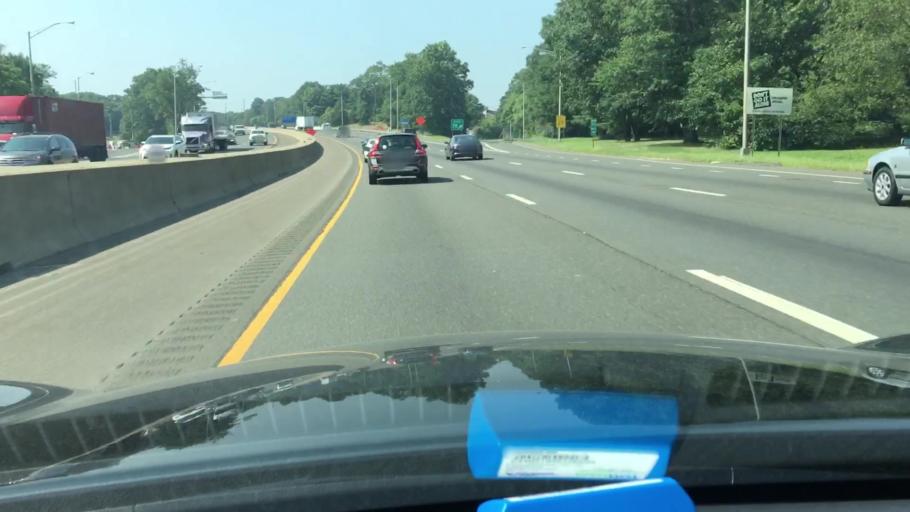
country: US
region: Connecticut
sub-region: New Haven County
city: City of Milford (balance)
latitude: 41.2152
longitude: -73.0861
